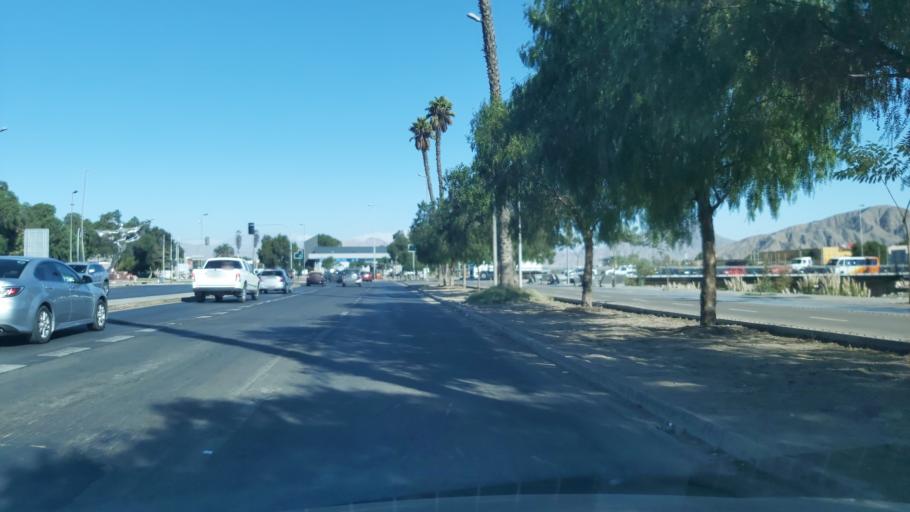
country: CL
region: Atacama
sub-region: Provincia de Copiapo
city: Copiapo
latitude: -27.3702
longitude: -70.3356
